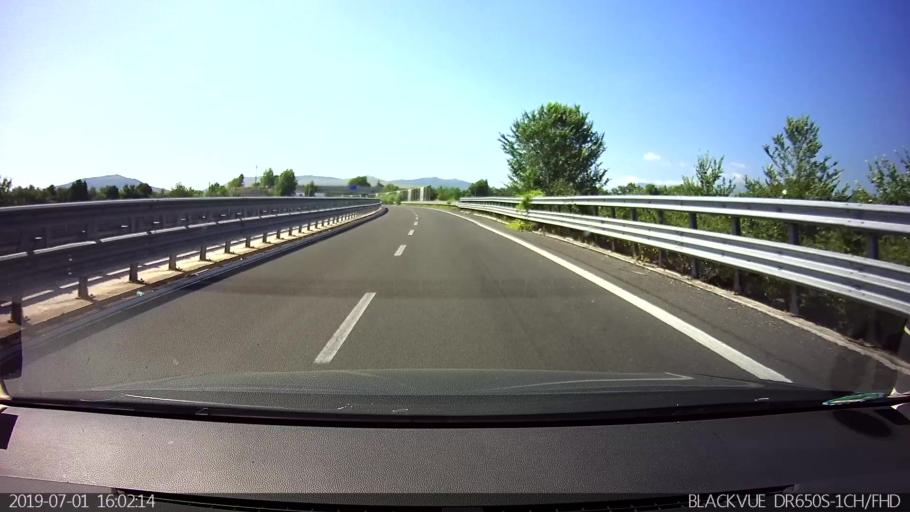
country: IT
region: Latium
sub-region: Provincia di Frosinone
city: Castelmassimo
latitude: 41.6682
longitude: 13.3604
